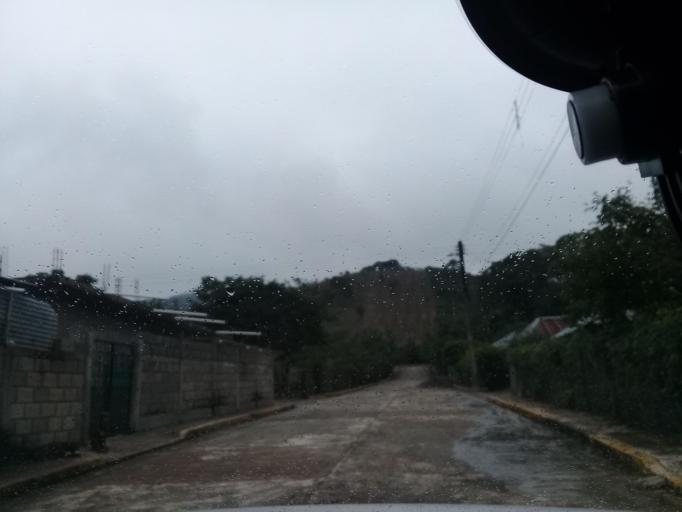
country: MX
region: Veracruz
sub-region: Chalma
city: San Pedro Coyutla
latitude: 21.2246
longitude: -98.4316
